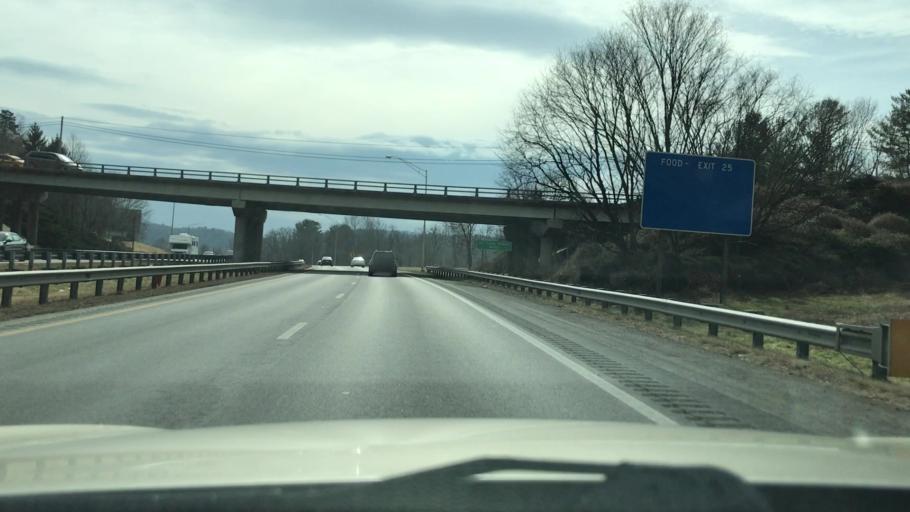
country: US
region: North Carolina
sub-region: Buncombe County
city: Woodfin
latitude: 35.6319
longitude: -82.5809
